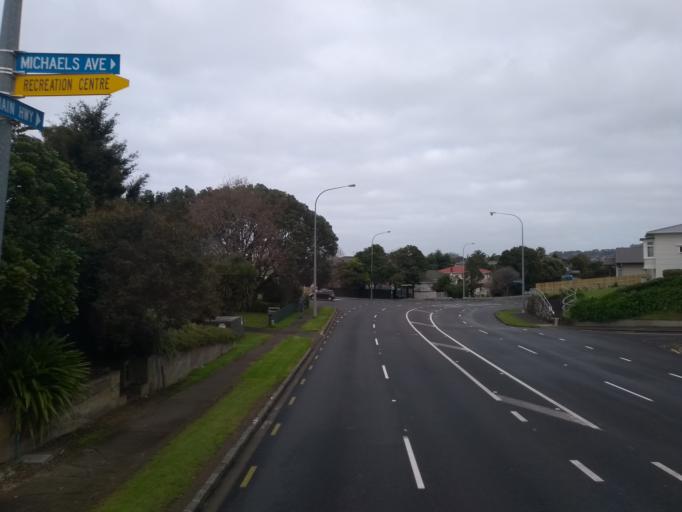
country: NZ
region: Auckland
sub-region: Auckland
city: Tamaki
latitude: -36.8991
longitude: 174.8204
